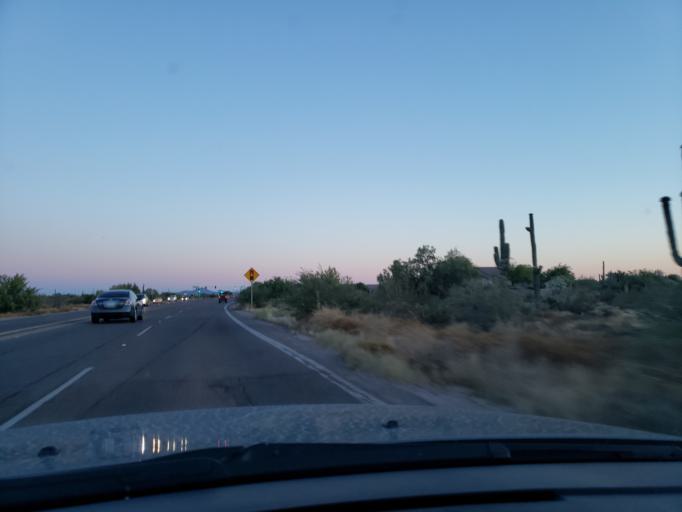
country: US
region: Arizona
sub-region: Maricopa County
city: Cave Creek
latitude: 33.7294
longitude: -111.9776
